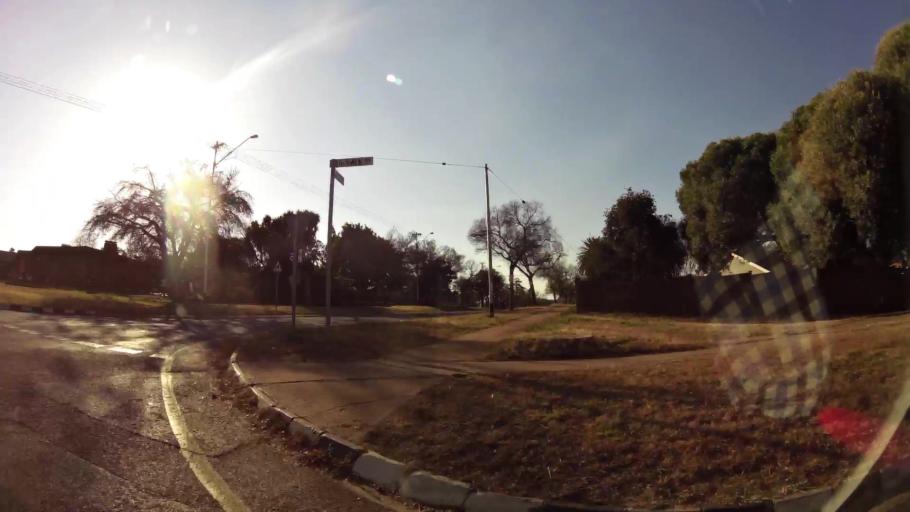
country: ZA
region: Gauteng
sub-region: City of Tshwane Metropolitan Municipality
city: Pretoria
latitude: -25.7549
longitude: 28.1407
